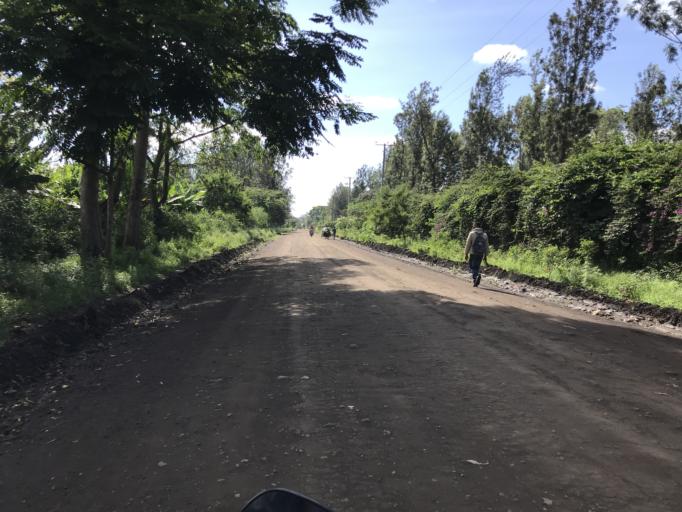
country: TZ
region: Arusha
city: Nkoaranga
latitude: -3.3783
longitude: 36.7910
